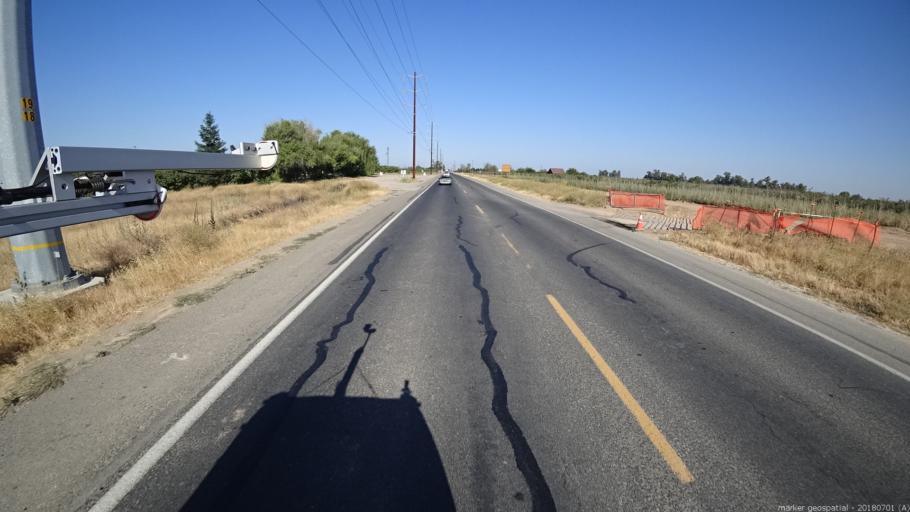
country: US
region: California
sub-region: Madera County
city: Parksdale
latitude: 36.9234
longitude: -119.9861
